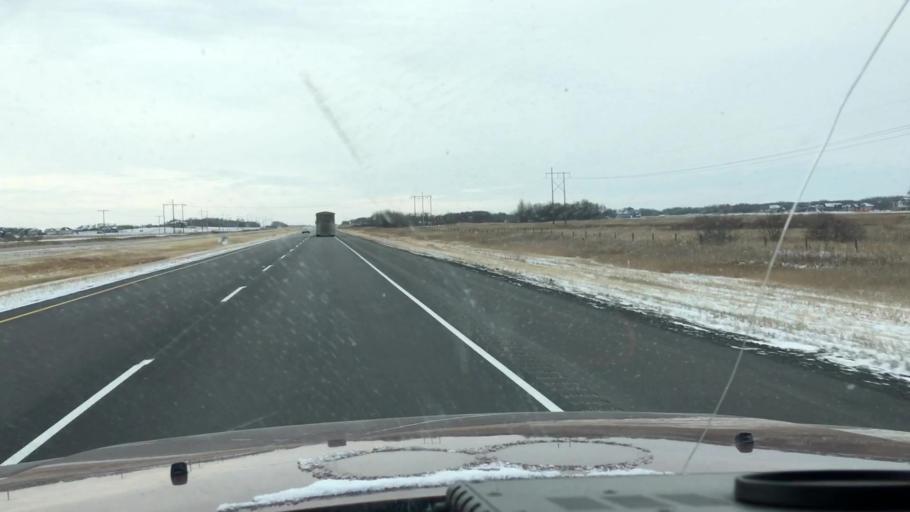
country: CA
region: Saskatchewan
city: Saskatoon
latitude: 51.9525
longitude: -106.5458
